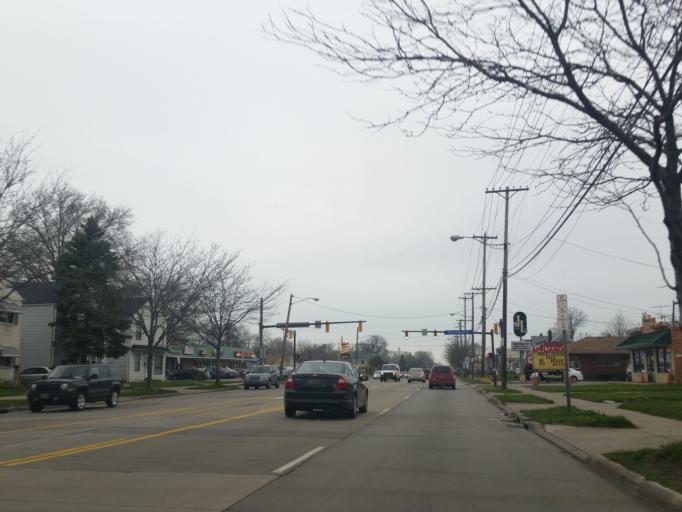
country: US
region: Ohio
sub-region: Cuyahoga County
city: Brooklyn
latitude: 41.4492
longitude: -81.7690
